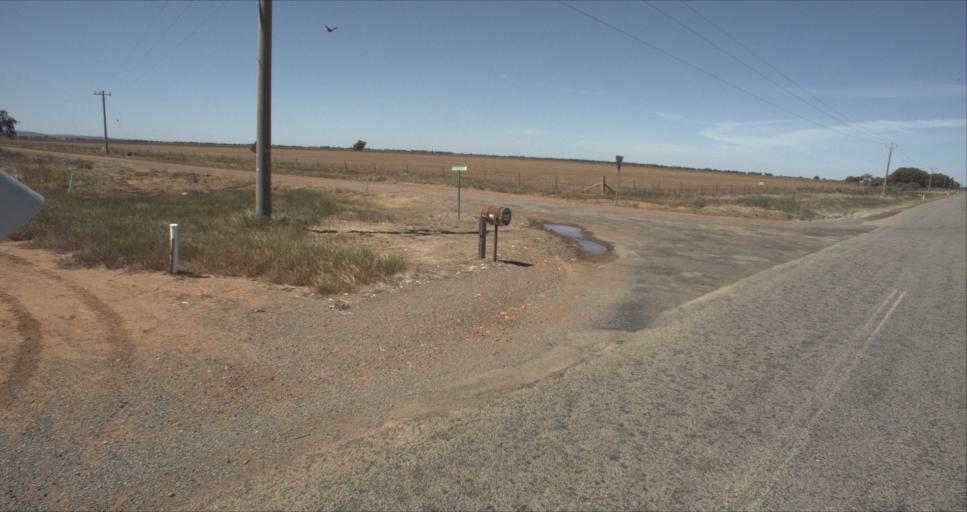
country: AU
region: New South Wales
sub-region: Leeton
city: Leeton
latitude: -34.4574
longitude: 146.2948
